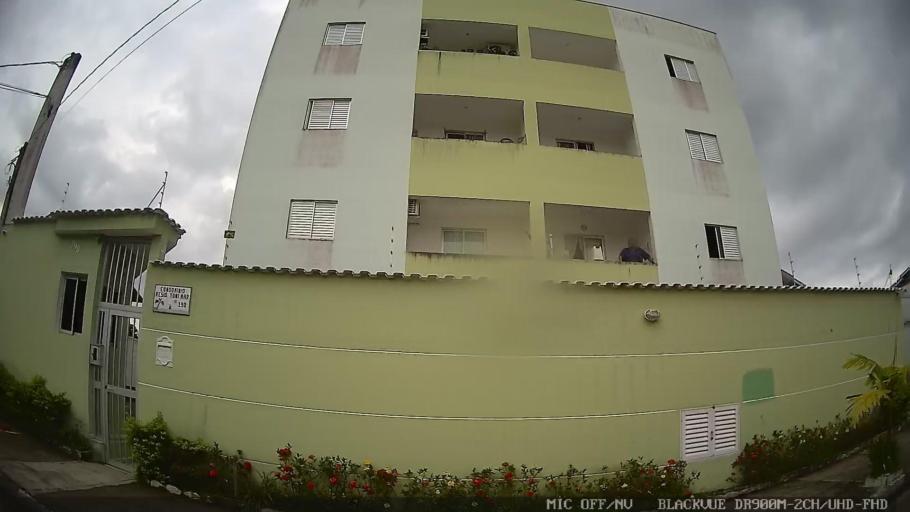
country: BR
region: Sao Paulo
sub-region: Caraguatatuba
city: Caraguatatuba
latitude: -23.6276
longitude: -45.3871
